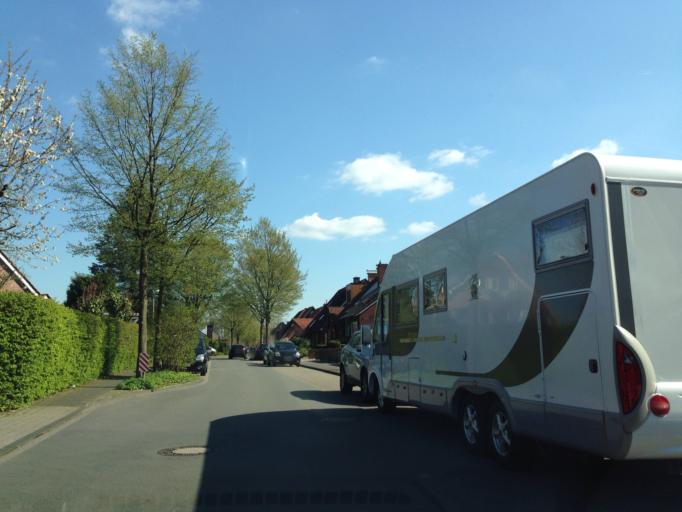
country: DE
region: North Rhine-Westphalia
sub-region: Regierungsbezirk Munster
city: Muenster
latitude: 51.9936
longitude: 7.5940
